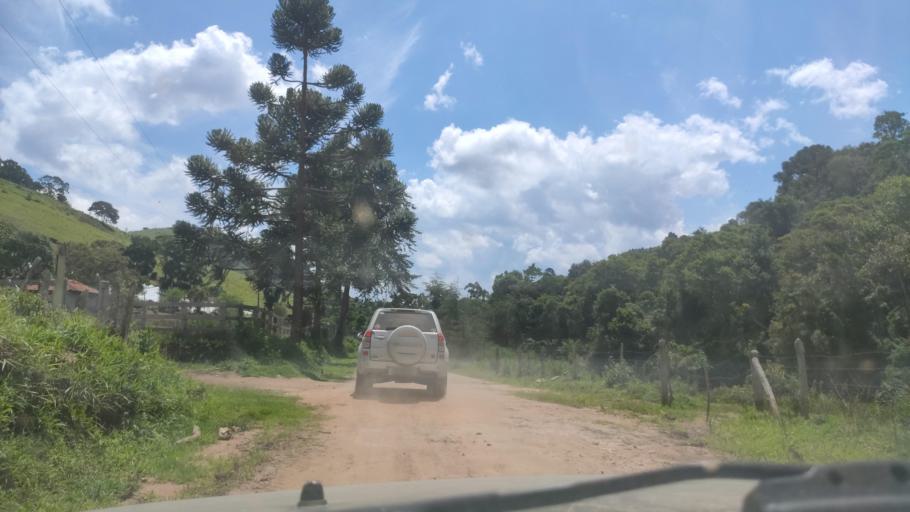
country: BR
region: Minas Gerais
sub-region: Cambui
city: Cambui
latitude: -22.6928
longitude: -45.9831
